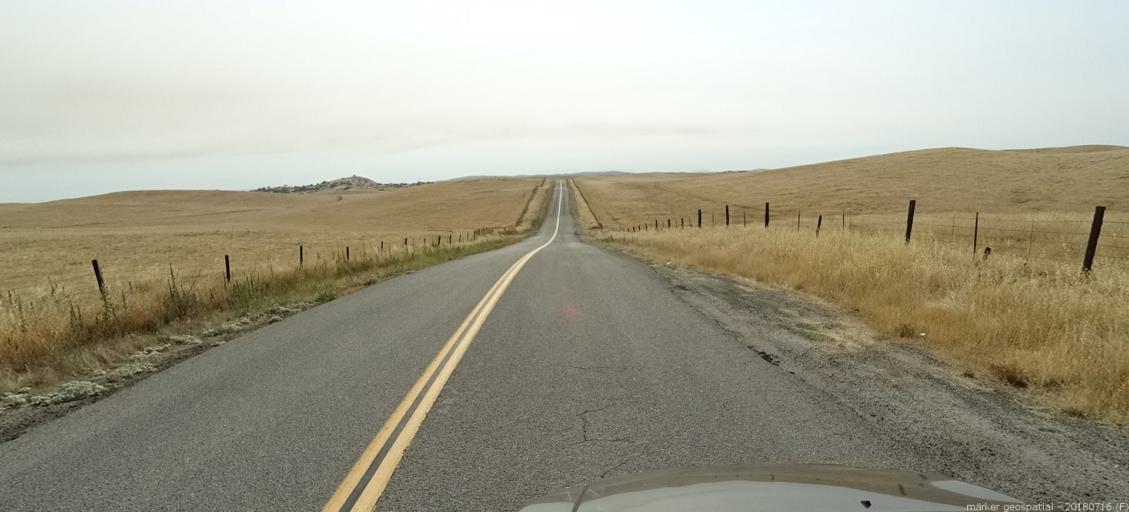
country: US
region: California
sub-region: Madera County
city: Madera Acres
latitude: 37.1193
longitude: -119.9625
